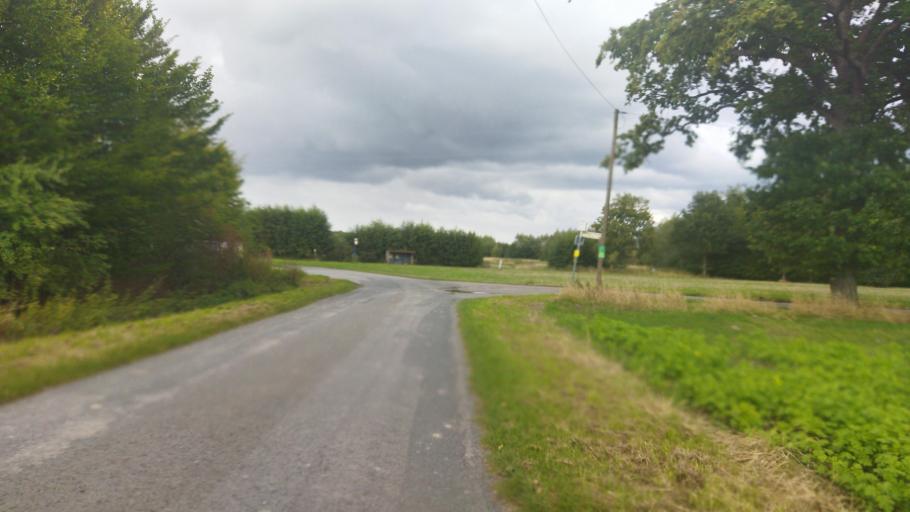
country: DE
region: North Rhine-Westphalia
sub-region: Regierungsbezirk Munster
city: Dulmen
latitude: 51.8863
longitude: 7.2648
